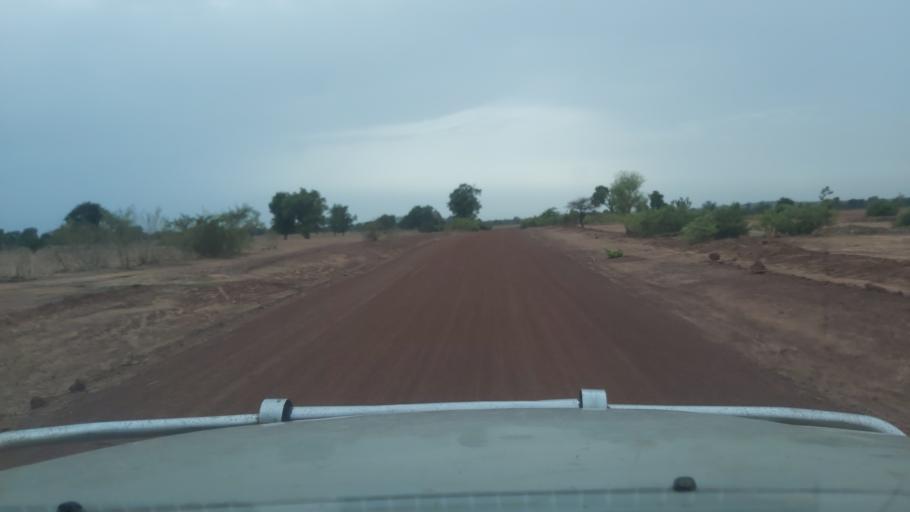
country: ML
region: Koulikoro
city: Banamba
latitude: 13.2747
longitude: -7.5425
